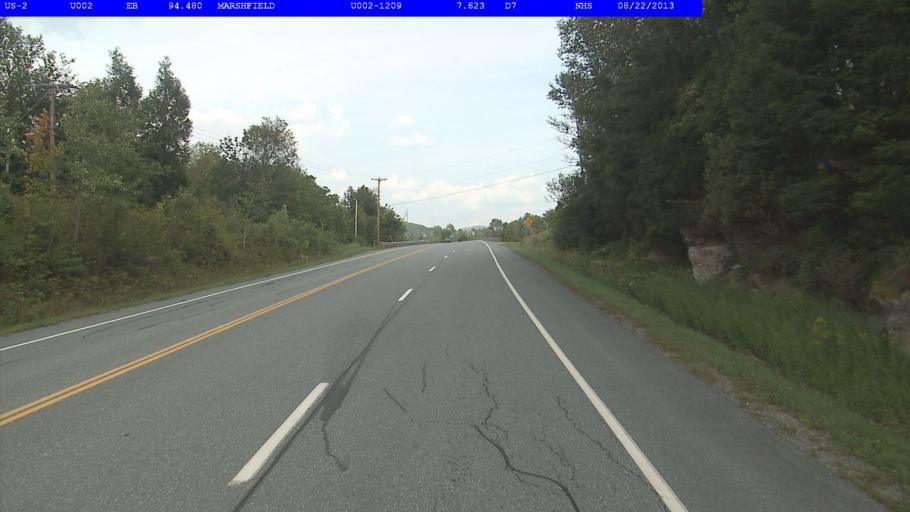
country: US
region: Vermont
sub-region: Caledonia County
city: Hardwick
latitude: 44.3576
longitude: -72.3339
